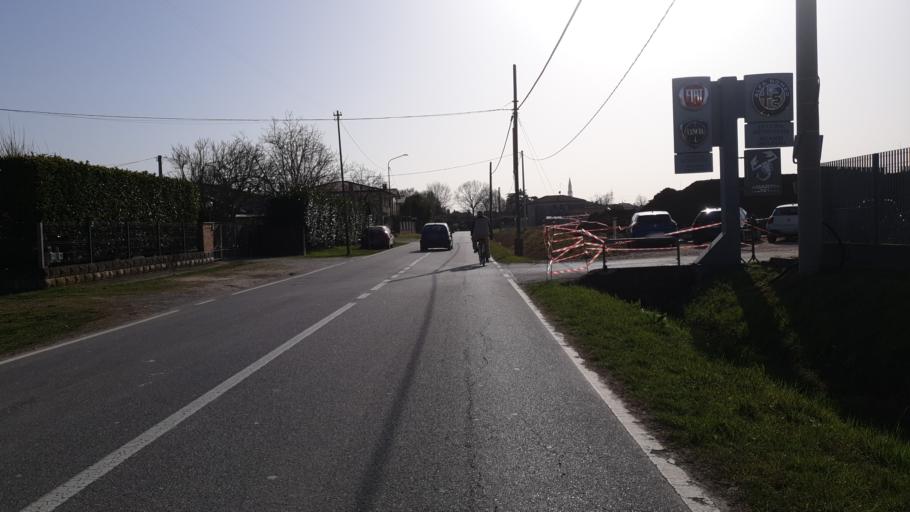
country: IT
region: Veneto
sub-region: Provincia di Padova
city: Vigodarzere
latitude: 45.4645
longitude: 11.8893
